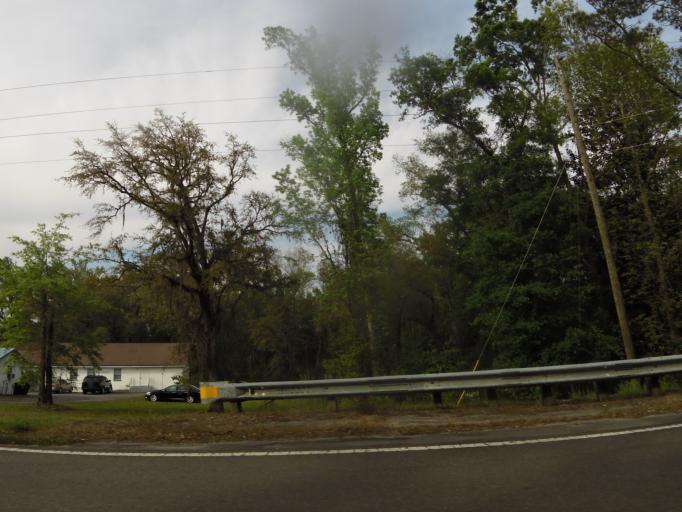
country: US
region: Georgia
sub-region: Camden County
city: Kingsland
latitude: 30.6997
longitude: -81.7477
